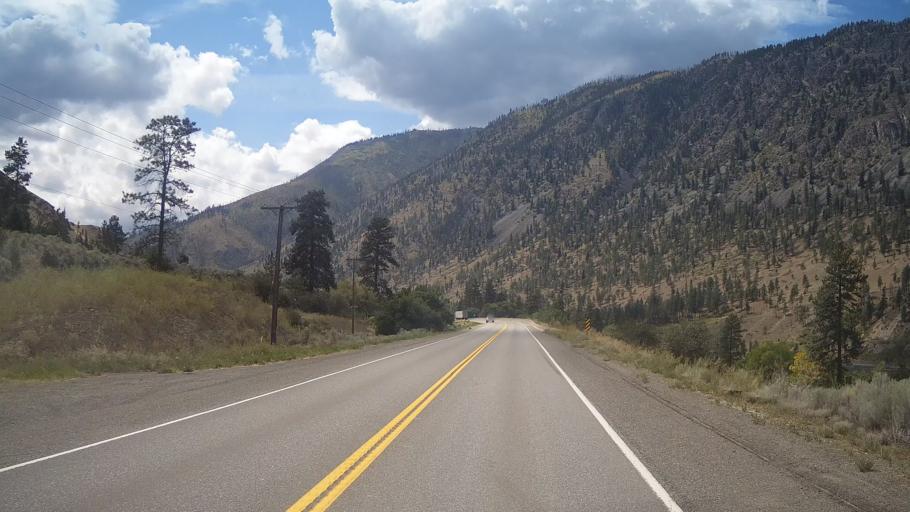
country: CA
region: British Columbia
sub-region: Thompson-Nicola Regional District
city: Ashcroft
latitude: 50.3430
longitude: -121.3922
